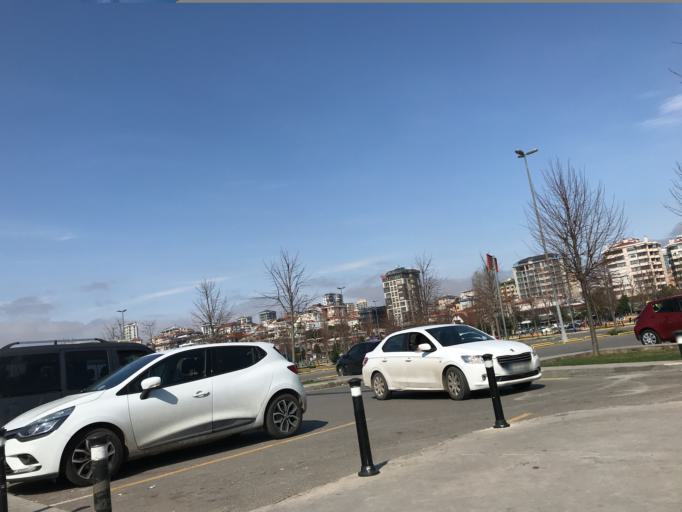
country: TR
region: Istanbul
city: Maltepe
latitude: 40.9257
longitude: 29.1216
